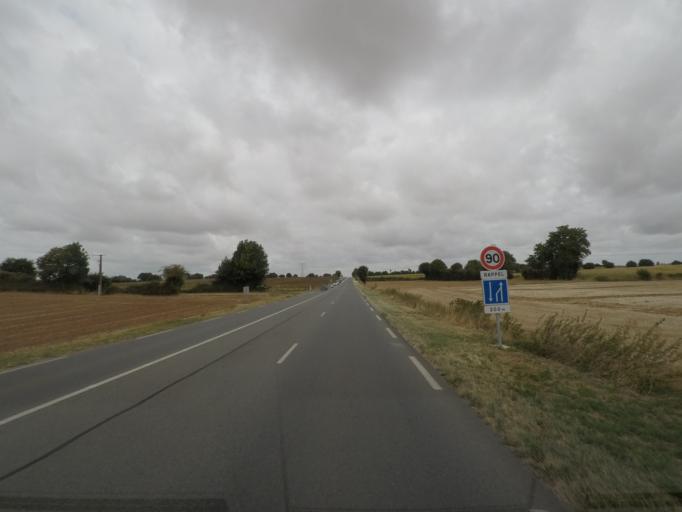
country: FR
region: Poitou-Charentes
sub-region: Departement des Deux-Sevres
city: Celles-sur-Belle
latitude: 46.2721
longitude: -0.2343
